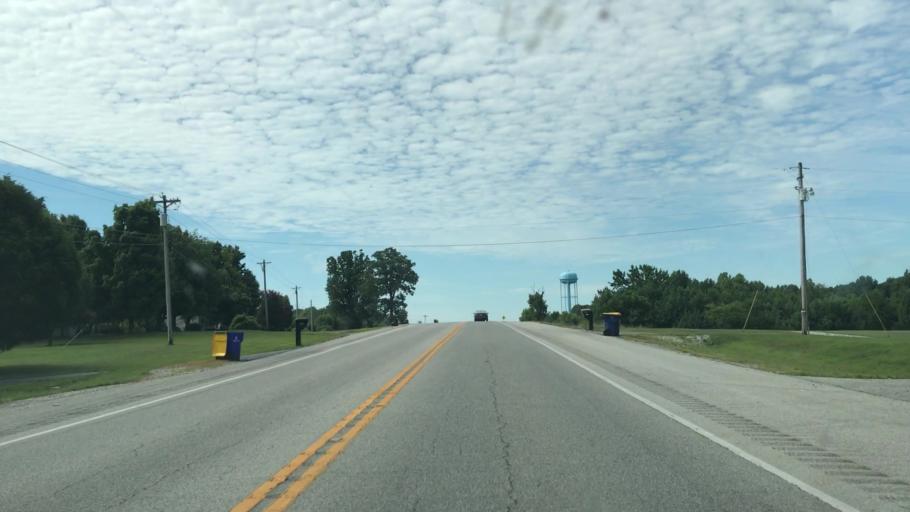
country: US
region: Kentucky
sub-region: Edmonson County
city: Brownsville
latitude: 37.1073
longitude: -86.2294
